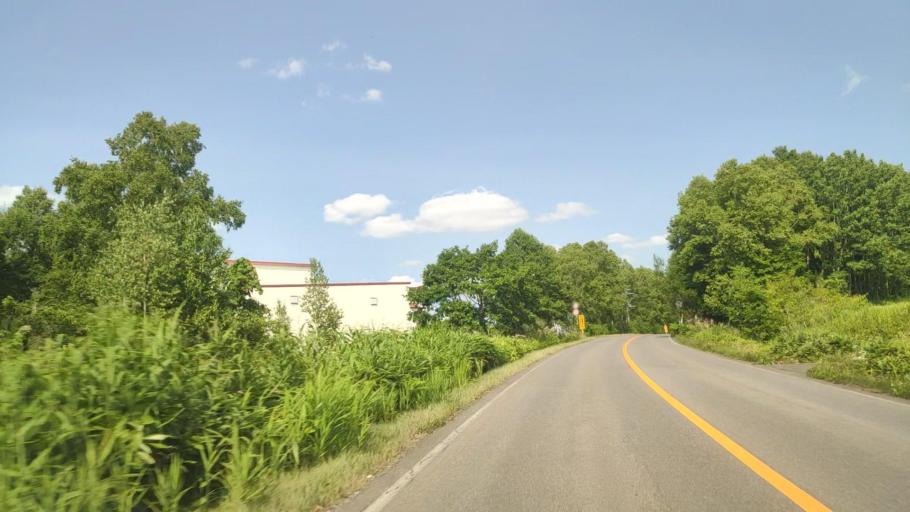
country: JP
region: Hokkaido
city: Nayoro
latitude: 44.2809
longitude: 142.4248
